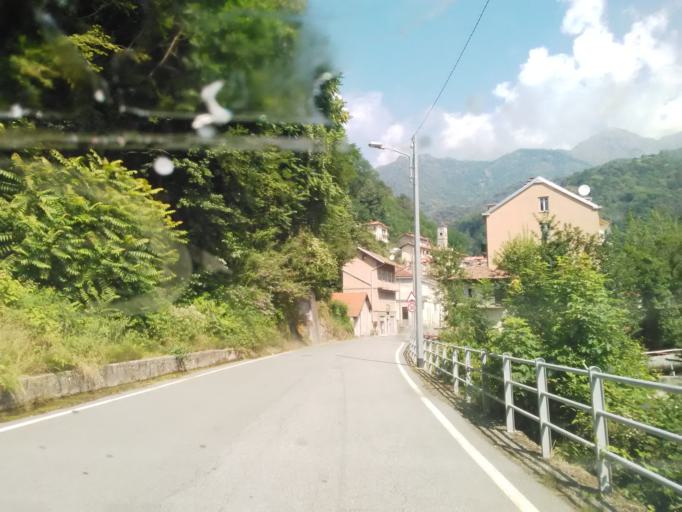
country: IT
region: Piedmont
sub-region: Provincia di Biella
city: Coggiola
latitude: 45.6884
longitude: 8.1723
